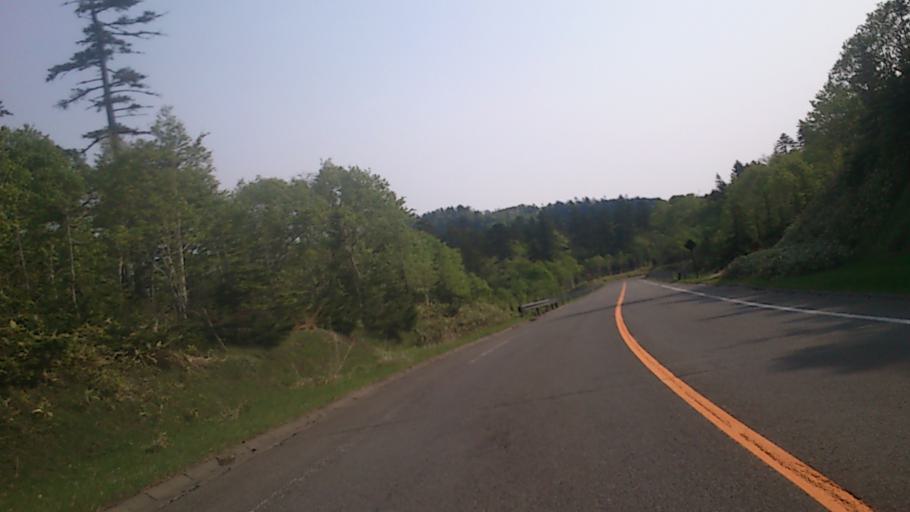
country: JP
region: Hokkaido
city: Bihoro
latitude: 43.4583
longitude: 144.2240
